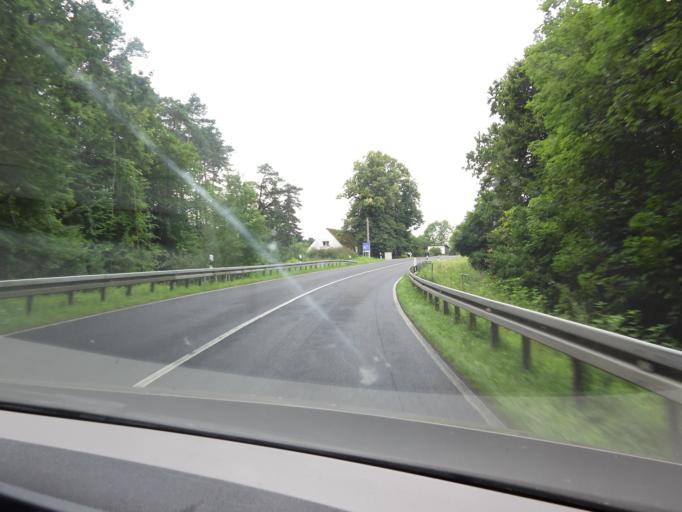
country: DE
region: Brandenburg
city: Lychen
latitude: 53.2098
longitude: 13.2788
